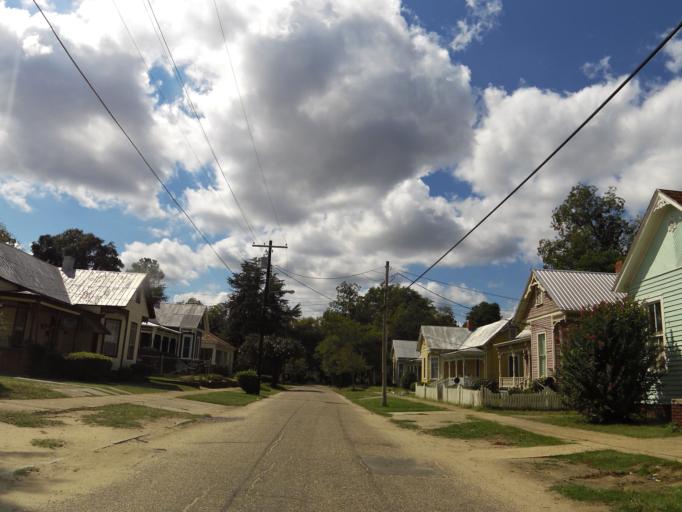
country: US
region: Alabama
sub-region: Dallas County
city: Selma
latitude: 32.4035
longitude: -87.0295
